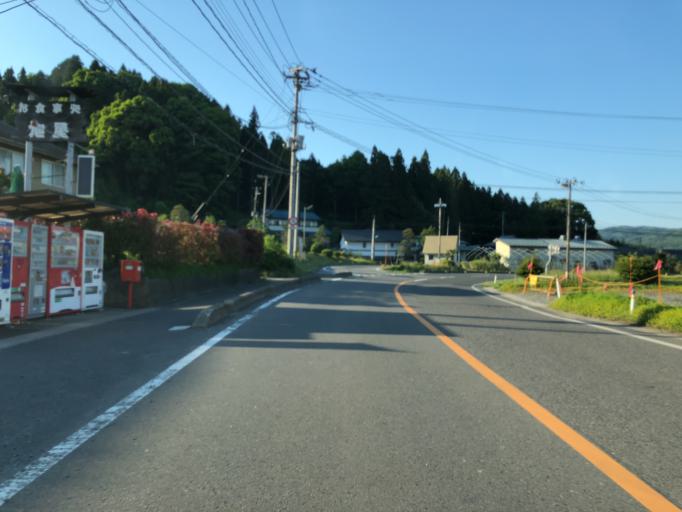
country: JP
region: Fukushima
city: Ishikawa
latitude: 36.9587
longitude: 140.4265
